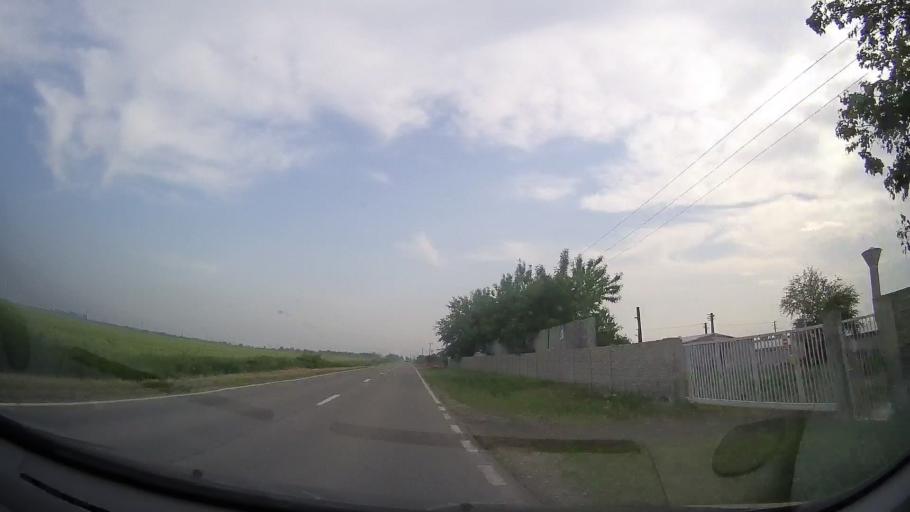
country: RO
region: Timis
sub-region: Comuna Parta
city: Parta
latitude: 45.6535
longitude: 21.1442
